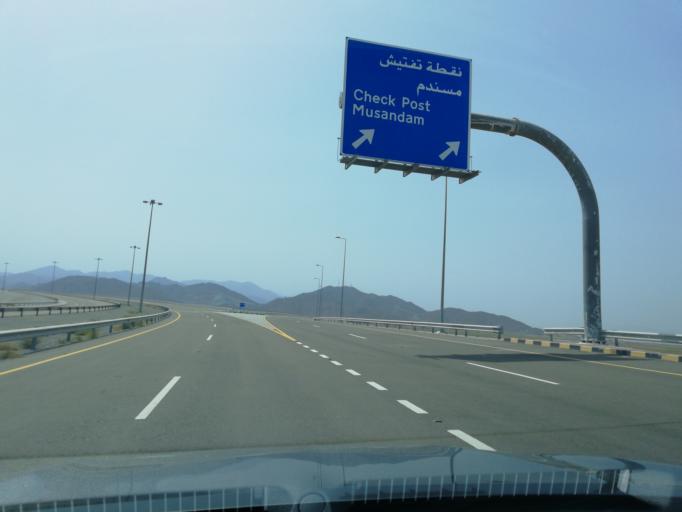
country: AE
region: Al Fujayrah
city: Al Fujayrah
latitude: 24.9529
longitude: 56.3775
